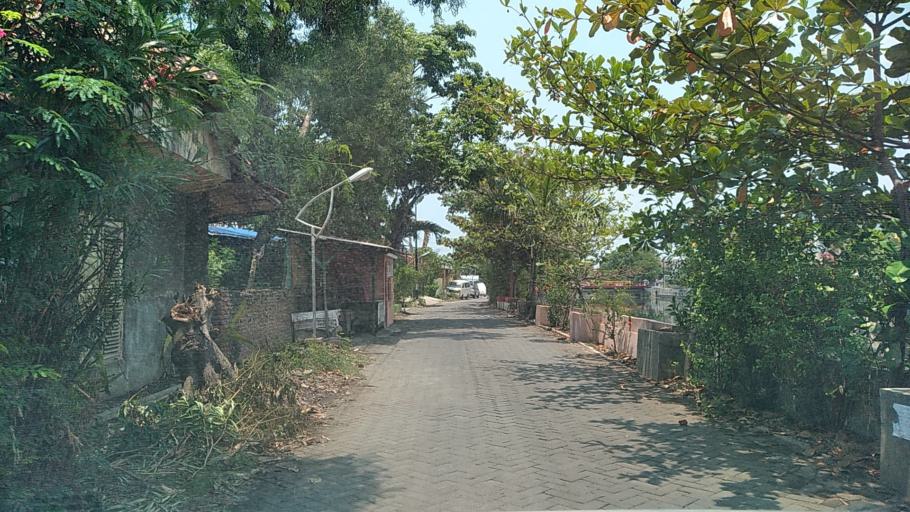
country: ID
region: Central Java
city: Semarang
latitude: -6.9681
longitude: 110.4392
